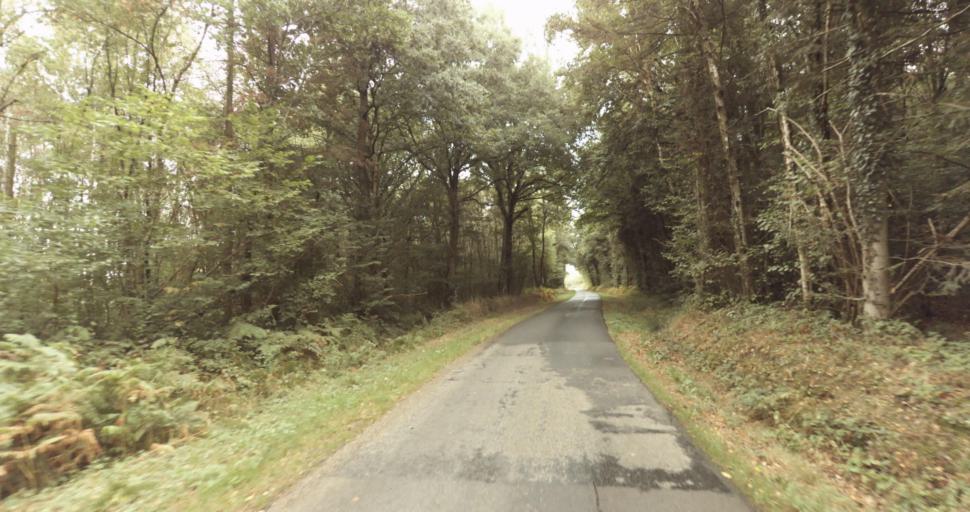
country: FR
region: Lower Normandy
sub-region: Departement de l'Orne
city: Gace
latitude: 48.8150
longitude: 0.3401
